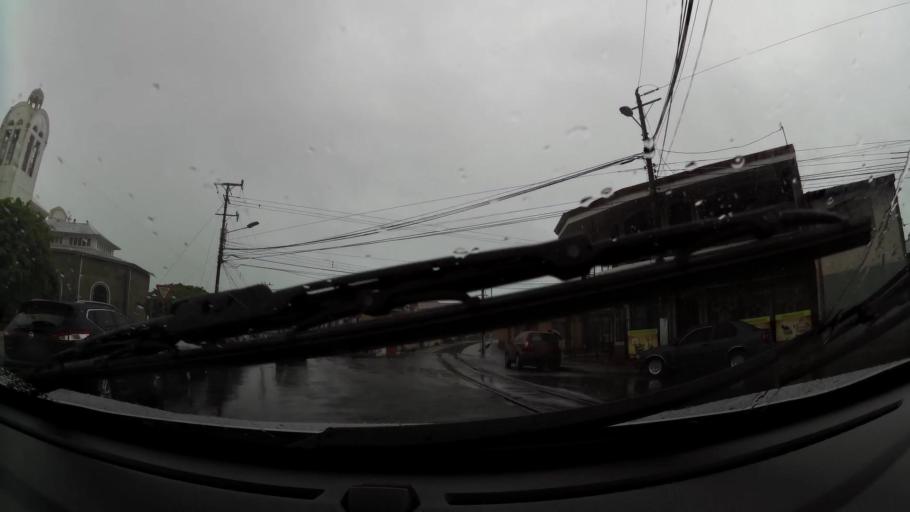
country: CR
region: Cartago
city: Cartago
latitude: 9.8645
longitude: -83.9125
